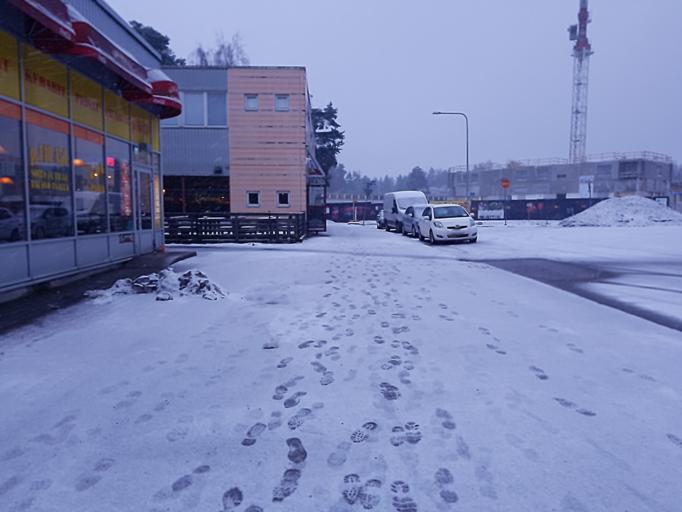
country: FI
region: Uusimaa
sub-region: Helsinki
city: Teekkarikylae
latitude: 60.2424
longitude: 24.8855
